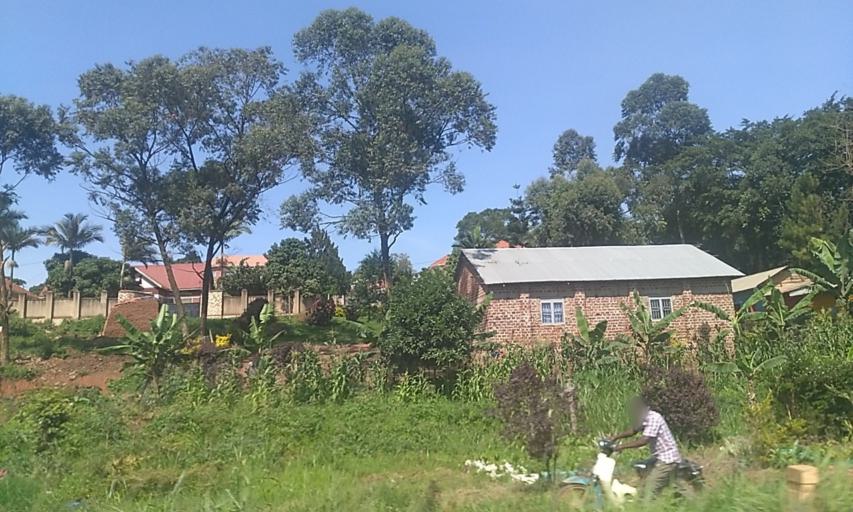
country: UG
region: Central Region
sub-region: Wakiso District
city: Kireka
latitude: 0.3618
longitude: 32.6502
